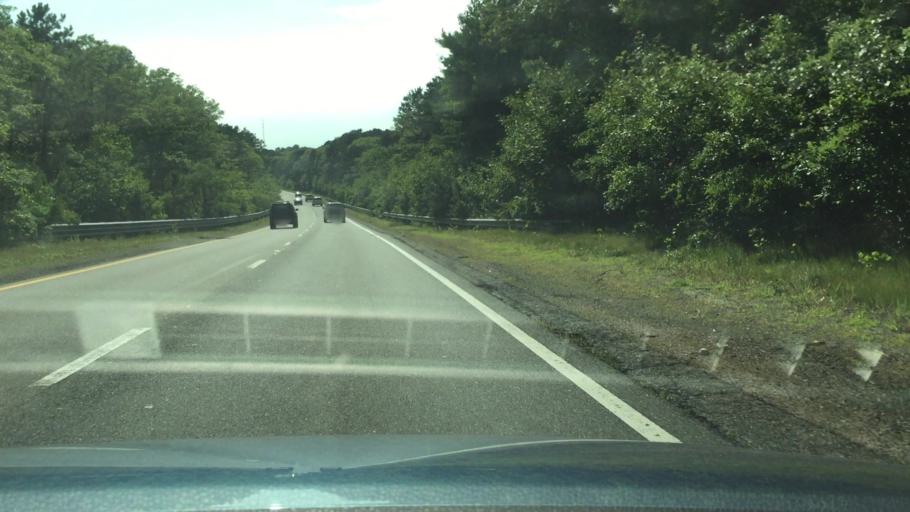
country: US
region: Massachusetts
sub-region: Barnstable County
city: Barnstable
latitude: 41.6906
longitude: -70.3213
